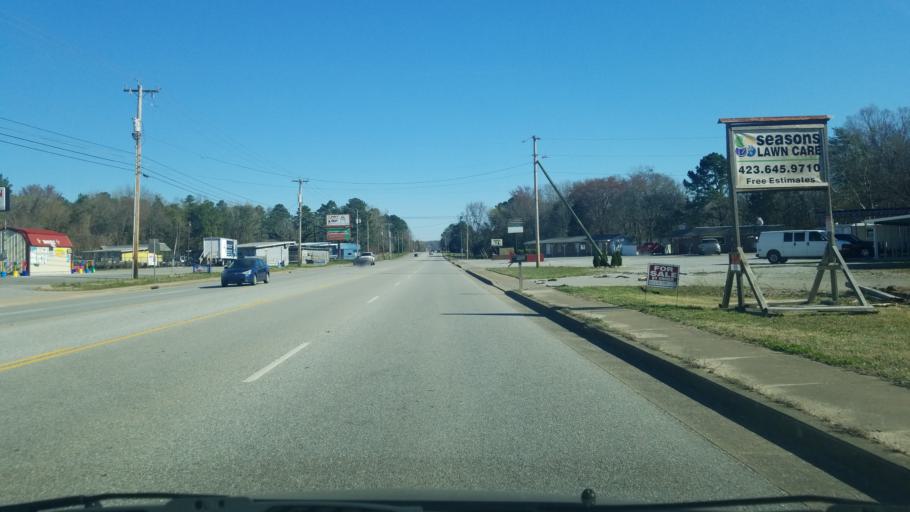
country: US
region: Tennessee
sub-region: Hamilton County
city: Middle Valley
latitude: 35.1759
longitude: -85.1717
